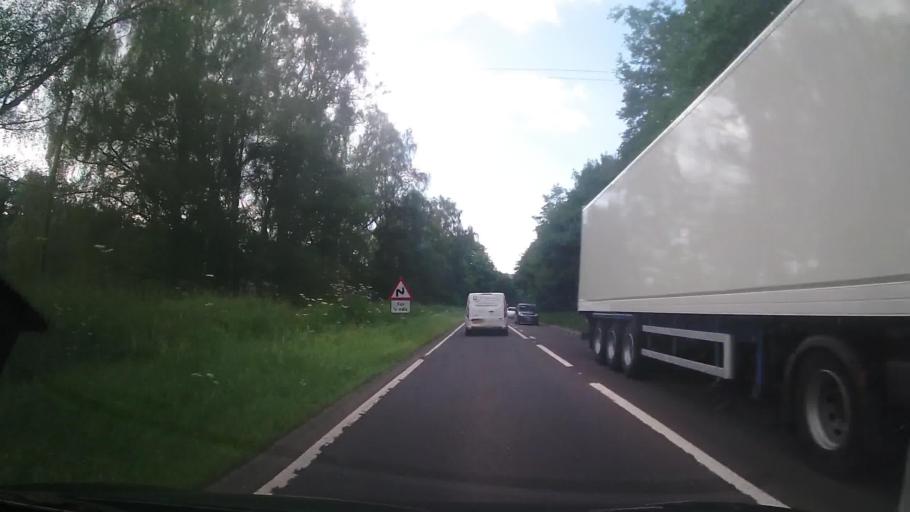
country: GB
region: England
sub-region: Shropshire
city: Church Stretton
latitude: 52.4978
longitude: -2.8179
